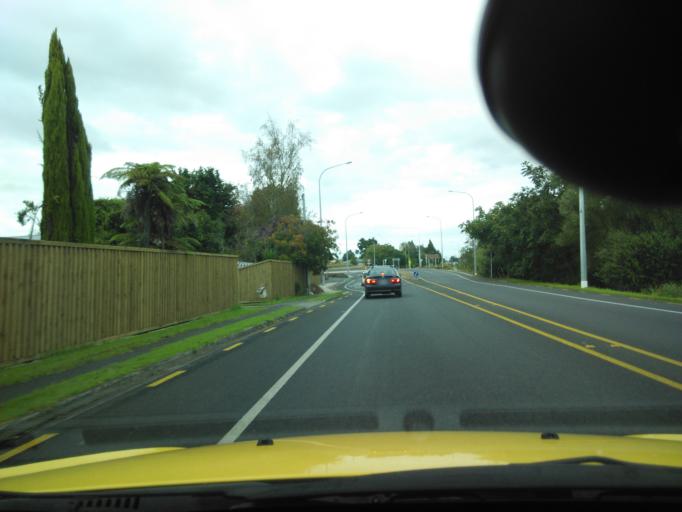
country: NZ
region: Waikato
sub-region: Waikato District
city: Ngaruawahia
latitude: -37.6104
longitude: 175.1857
